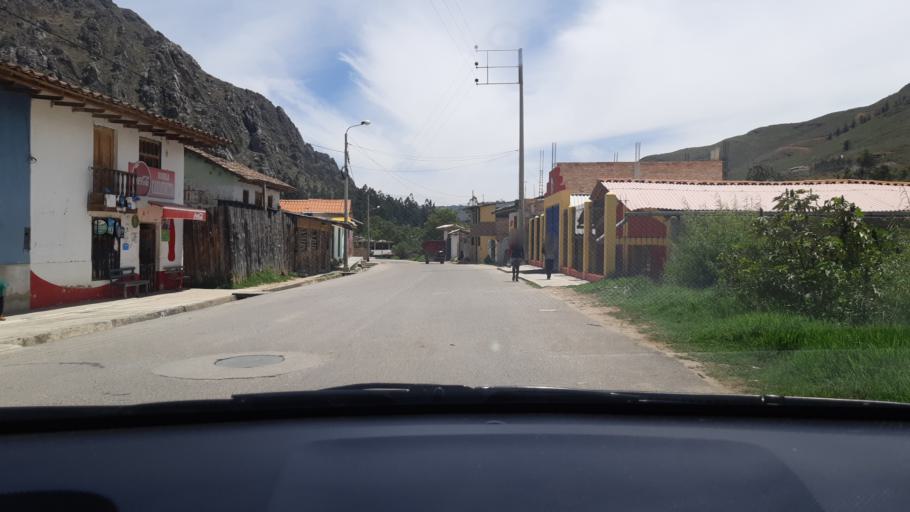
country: PE
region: Cajamarca
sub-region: Provincia de Cajamarca
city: Llacanora
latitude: -7.1829
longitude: -78.4489
